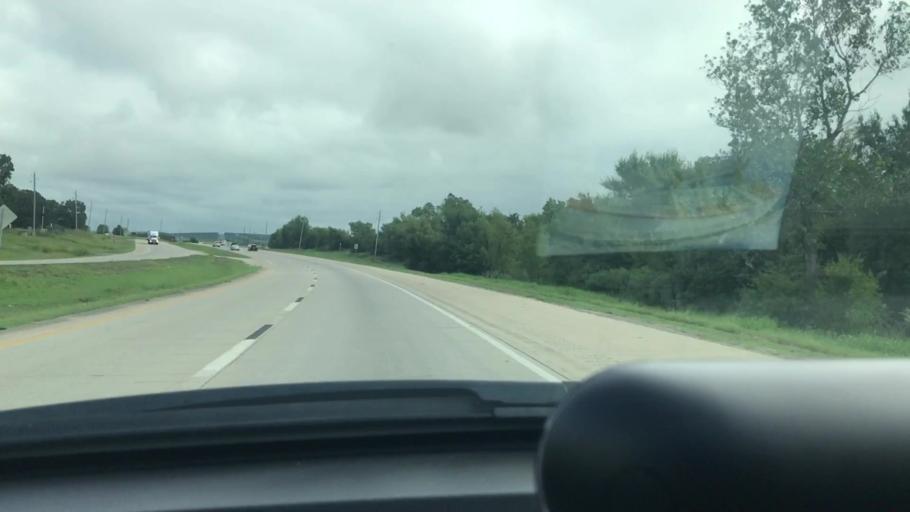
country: US
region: Oklahoma
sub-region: Atoka County
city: Atoka
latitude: 34.4010
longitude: -96.1163
